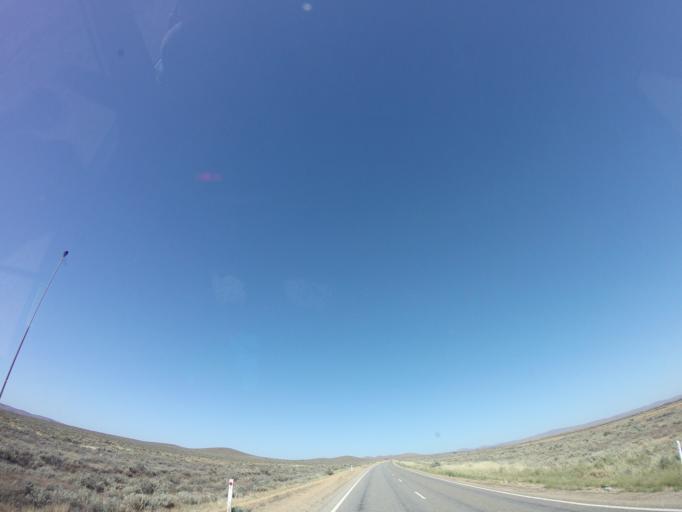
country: AU
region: South Australia
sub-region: Peterborough
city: Peterborough
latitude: -32.5408
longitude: 139.6654
